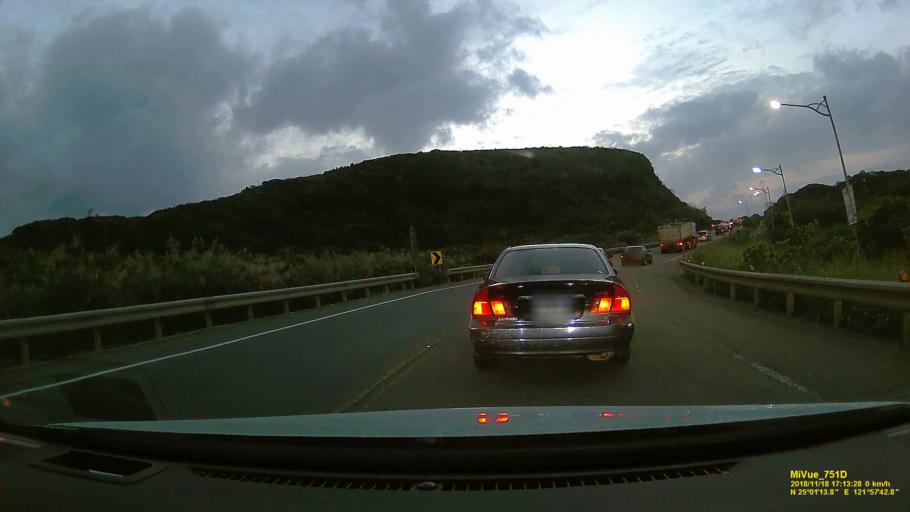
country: TW
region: Taiwan
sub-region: Keelung
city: Keelung
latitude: 25.0205
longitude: 121.9619
